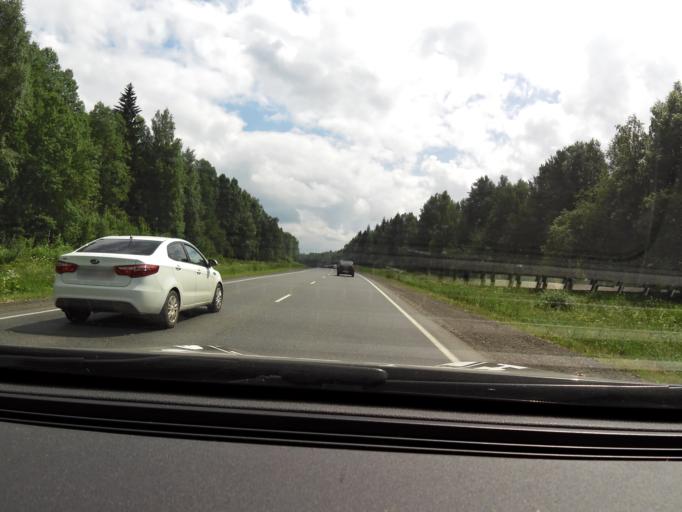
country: RU
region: Perm
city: Kungur
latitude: 57.4283
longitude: 56.8322
